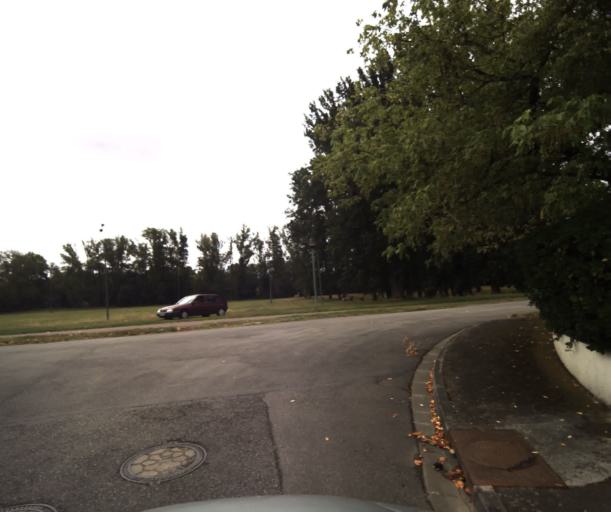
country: FR
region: Midi-Pyrenees
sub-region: Departement de la Haute-Garonne
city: Portet-sur-Garonne
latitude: 43.5185
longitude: 1.4040
